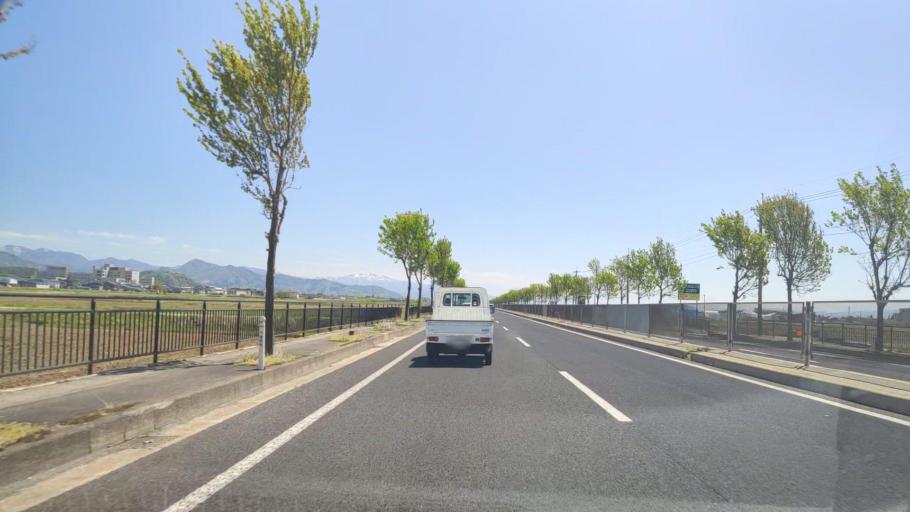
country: JP
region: Yamagata
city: Higashine
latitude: 38.4691
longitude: 140.3827
